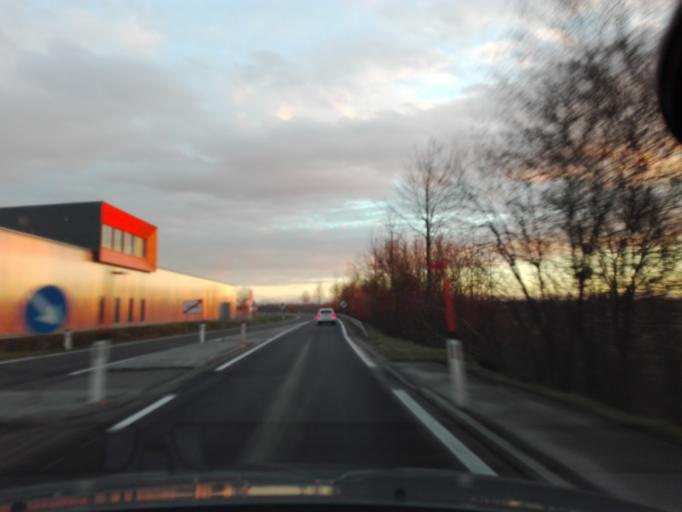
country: AT
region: Upper Austria
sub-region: Politischer Bezirk Perg
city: Perg
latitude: 48.2265
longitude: 14.7029
